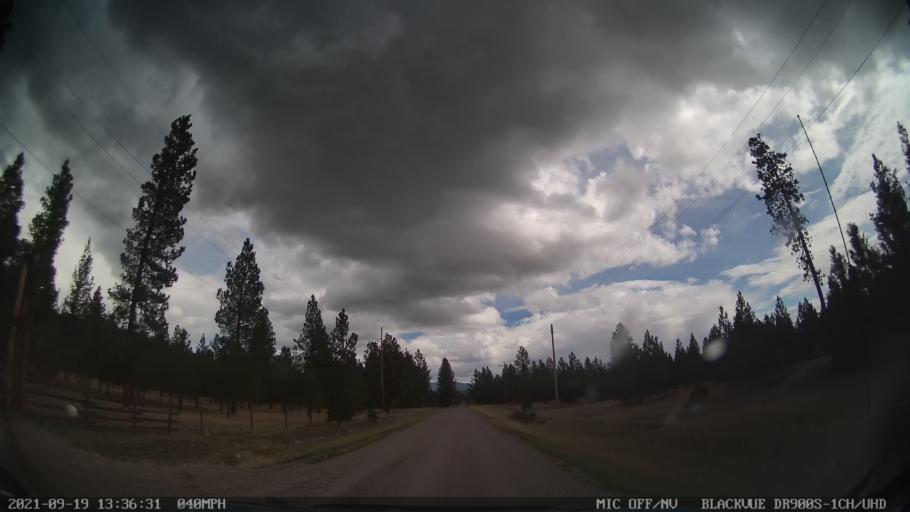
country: US
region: Montana
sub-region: Missoula County
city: Seeley Lake
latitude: 47.1066
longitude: -113.2968
